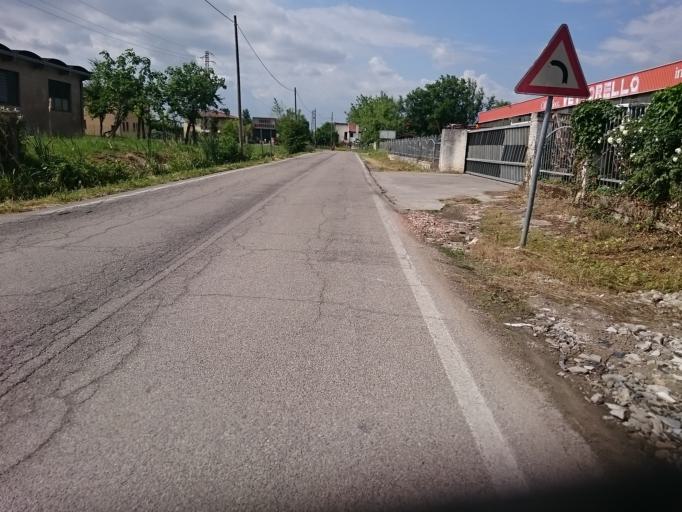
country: IT
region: Veneto
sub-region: Provincia di Padova
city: Casale di Scodosia
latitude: 45.1926
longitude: 11.4933
